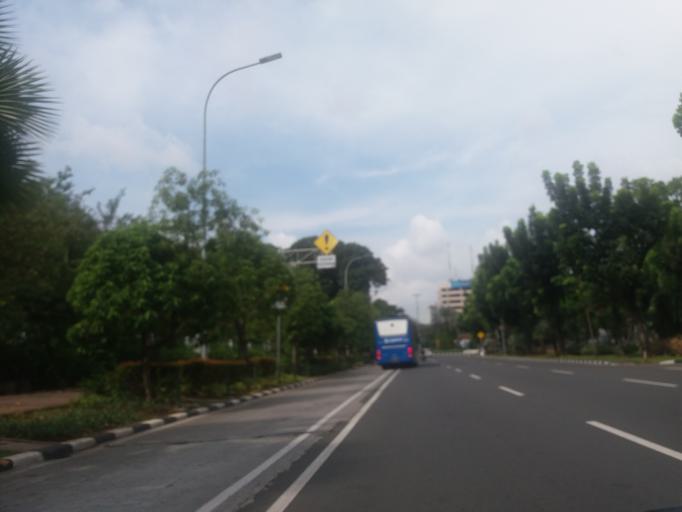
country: ID
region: Jakarta Raya
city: Jakarta
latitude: -6.1802
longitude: 106.8298
